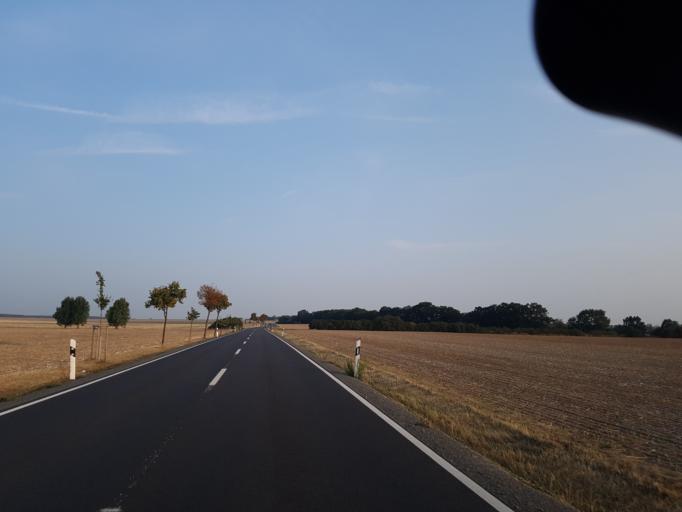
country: DE
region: Saxony
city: Zinna
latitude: 51.5820
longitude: 12.9593
